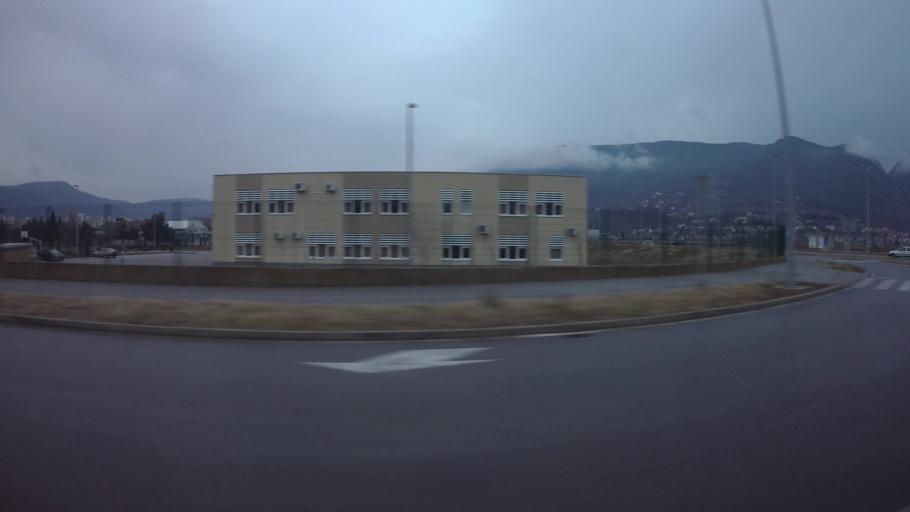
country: BA
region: Federation of Bosnia and Herzegovina
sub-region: Hercegovacko-Bosanski Kanton
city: Mostar
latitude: 43.3574
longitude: 17.8128
